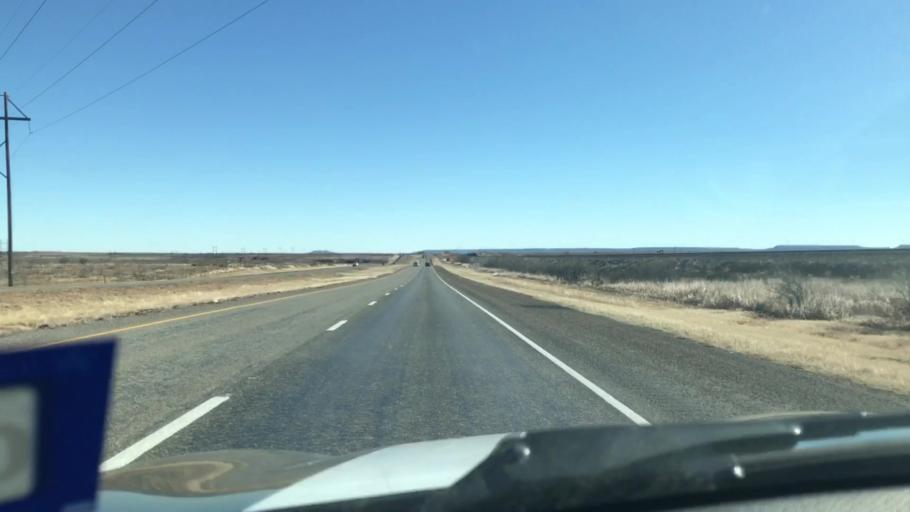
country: US
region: Texas
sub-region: Garza County
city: Post
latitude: 33.1164
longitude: -101.2769
